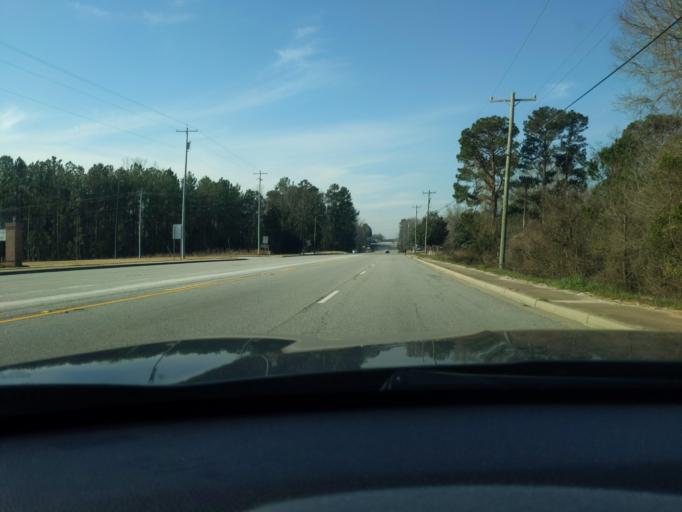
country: US
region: South Carolina
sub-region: Abbeville County
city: Abbeville
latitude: 34.1569
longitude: -82.3885
